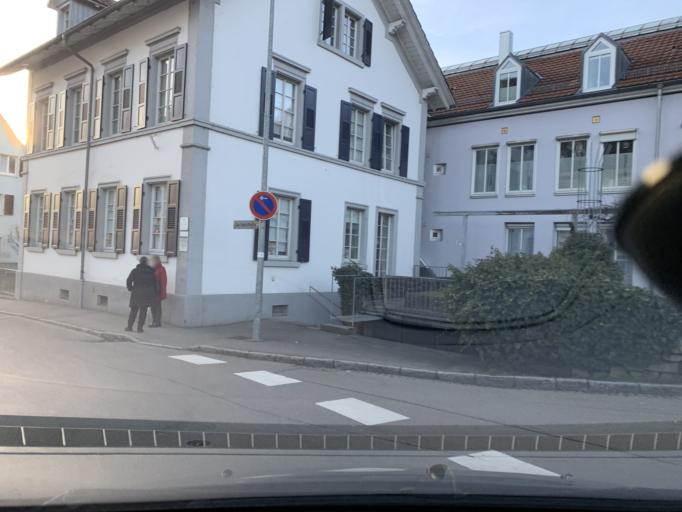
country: DE
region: Baden-Wuerttemberg
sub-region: Freiburg Region
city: Waldshut-Tiengen
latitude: 47.6250
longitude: 8.2121
